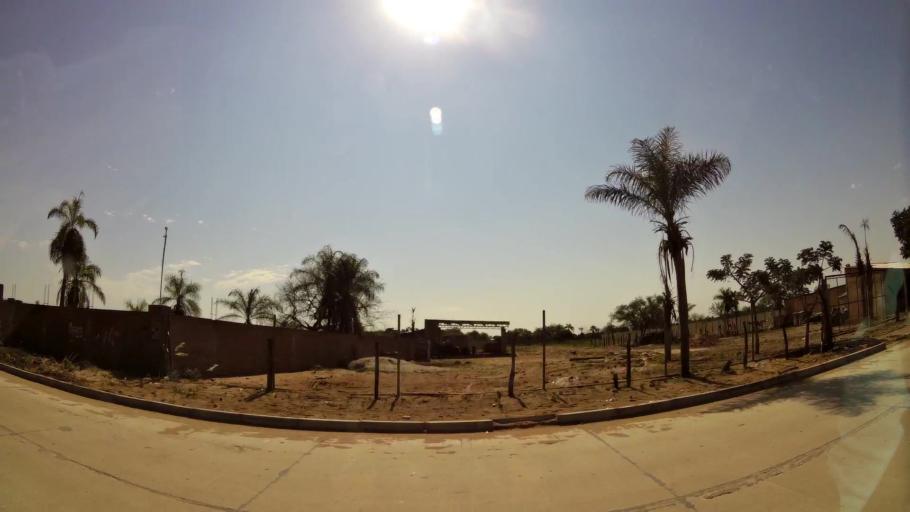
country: BO
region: Santa Cruz
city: Cotoca
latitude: -17.7133
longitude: -63.0671
